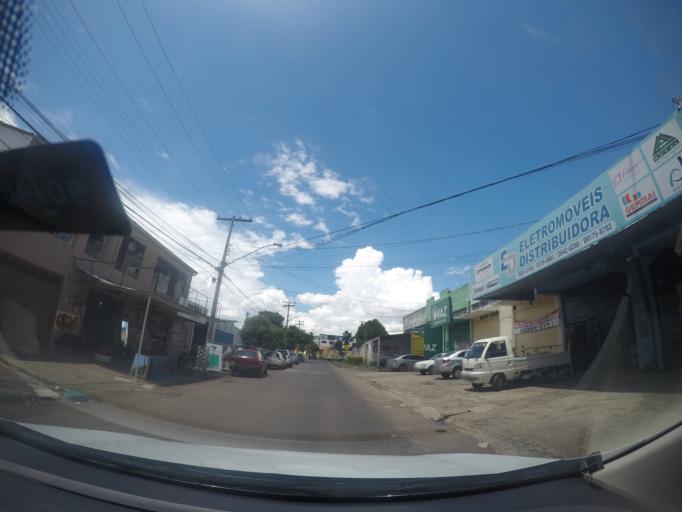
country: BR
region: Goias
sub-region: Goiania
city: Goiania
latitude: -16.7149
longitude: -49.2987
